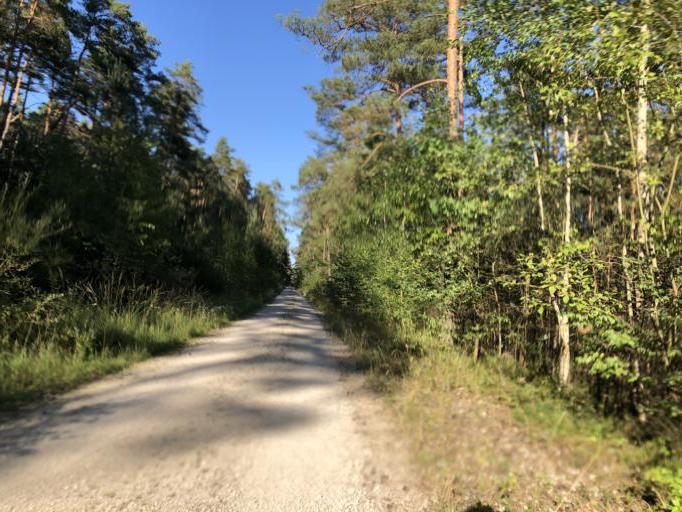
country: DE
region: Bavaria
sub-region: Regierungsbezirk Mittelfranken
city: Buckenhof
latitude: 49.5416
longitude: 11.0543
